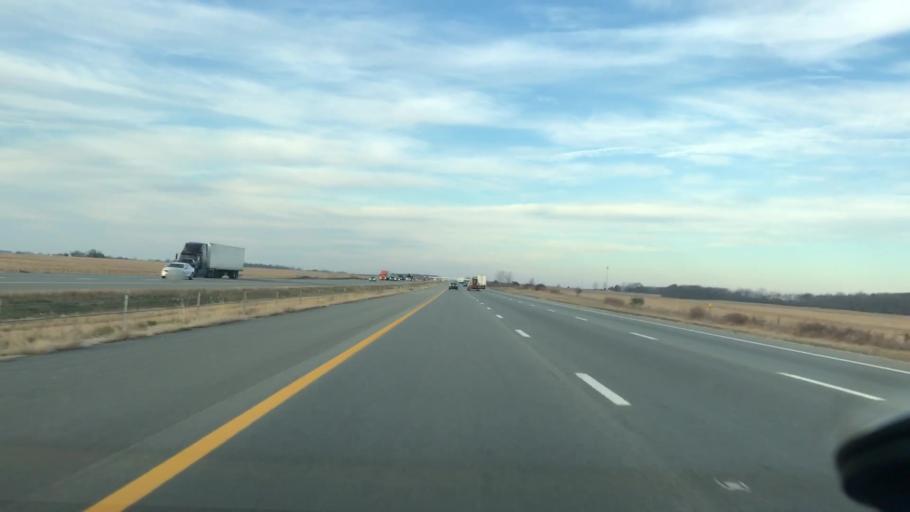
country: US
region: Ohio
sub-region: Madison County
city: Choctaw Lake
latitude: 39.9420
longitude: -83.4542
